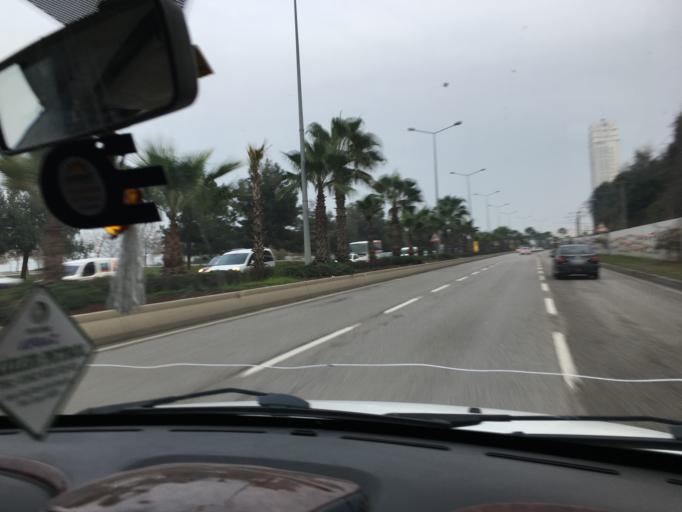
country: TR
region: Samsun
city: Samsun
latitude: 41.3174
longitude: 36.3323
